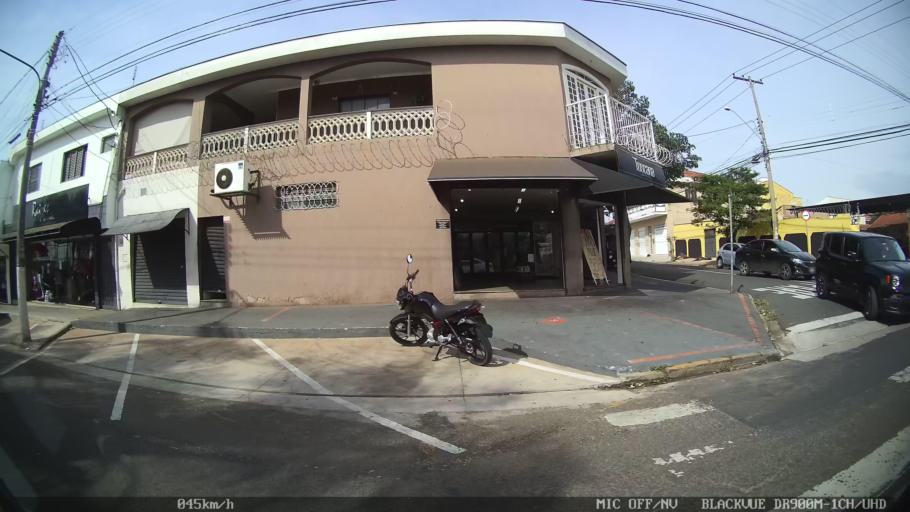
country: BR
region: Sao Paulo
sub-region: Piracicaba
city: Piracicaba
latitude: -22.7356
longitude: -47.6637
